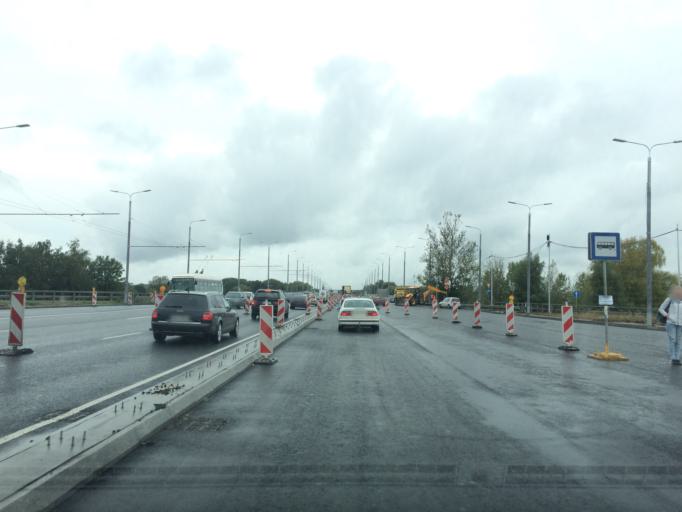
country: LV
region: Riga
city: Riga
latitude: 56.9328
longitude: 24.1200
